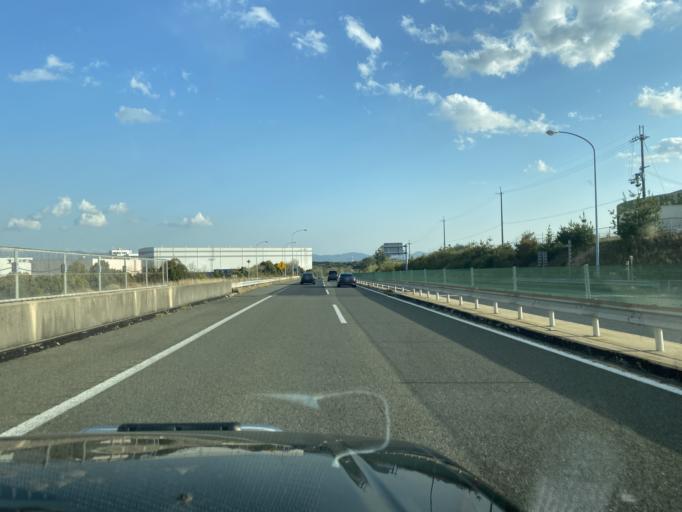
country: JP
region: Hyogo
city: Sandacho
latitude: 34.9312
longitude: 135.1589
